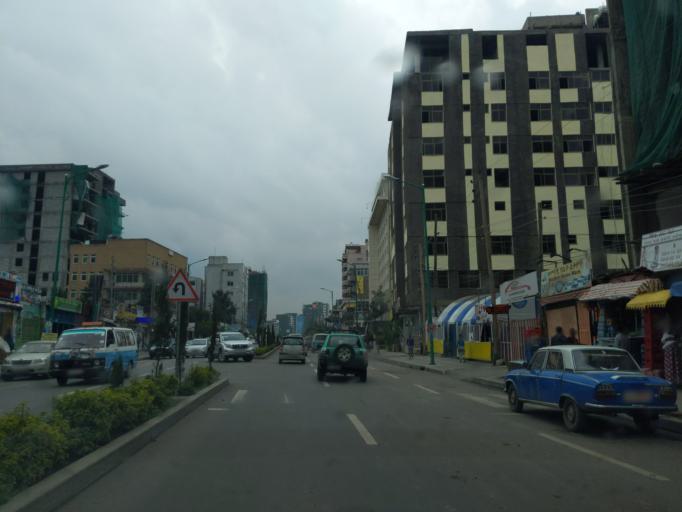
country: ET
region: Adis Abeba
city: Addis Ababa
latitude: 8.9941
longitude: 38.7666
